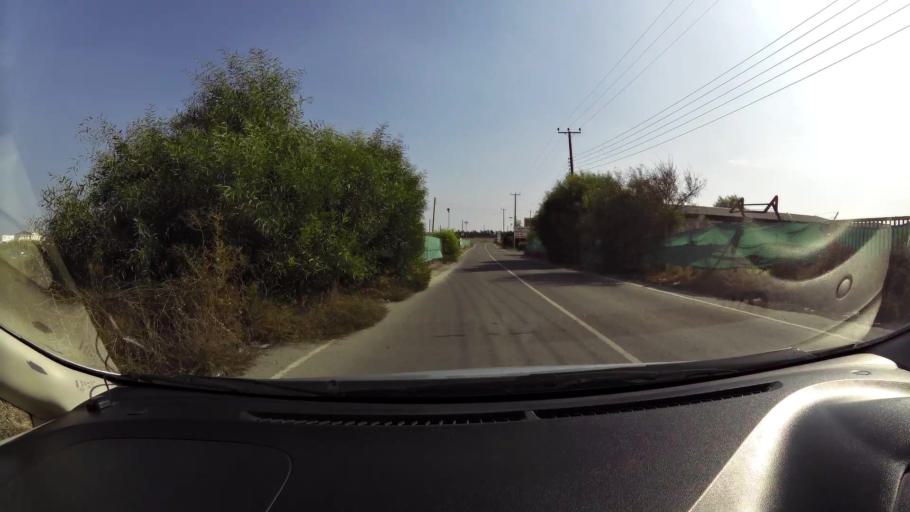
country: CY
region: Larnaka
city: Dhromolaxia
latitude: 34.9031
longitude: 33.5785
